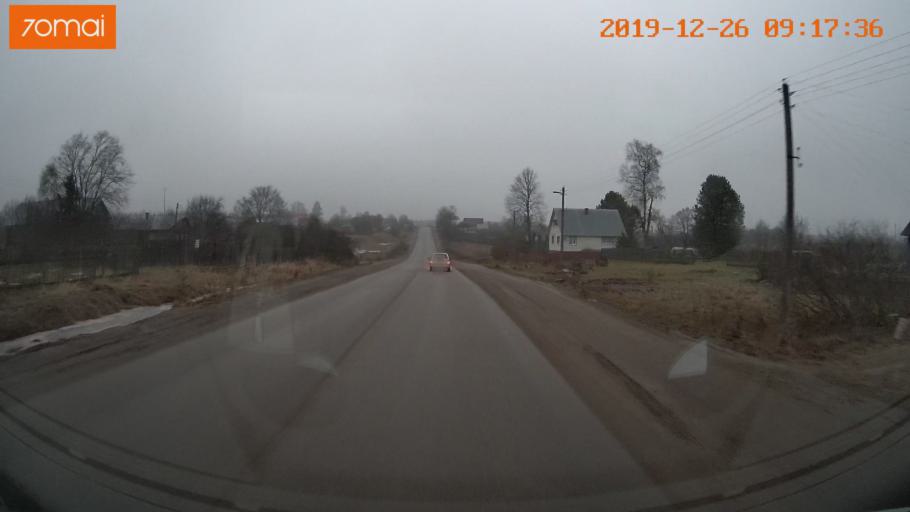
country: RU
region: Vologda
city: Gryazovets
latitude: 58.9313
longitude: 40.2405
